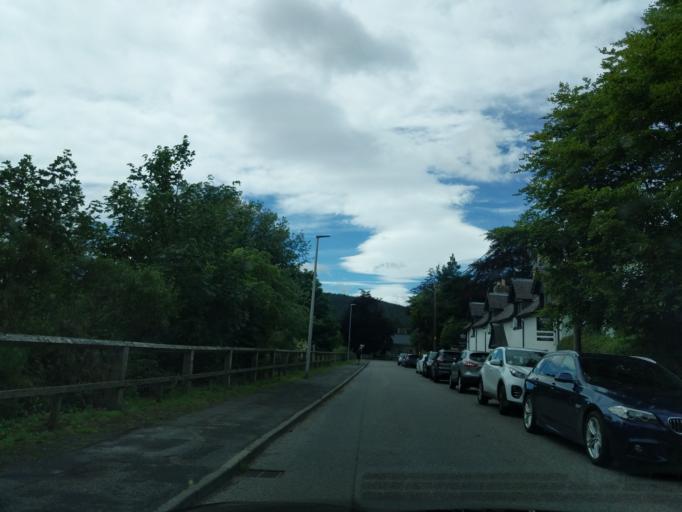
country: GB
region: Scotland
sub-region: Aberdeenshire
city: Aboyne
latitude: 57.0710
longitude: -2.7860
